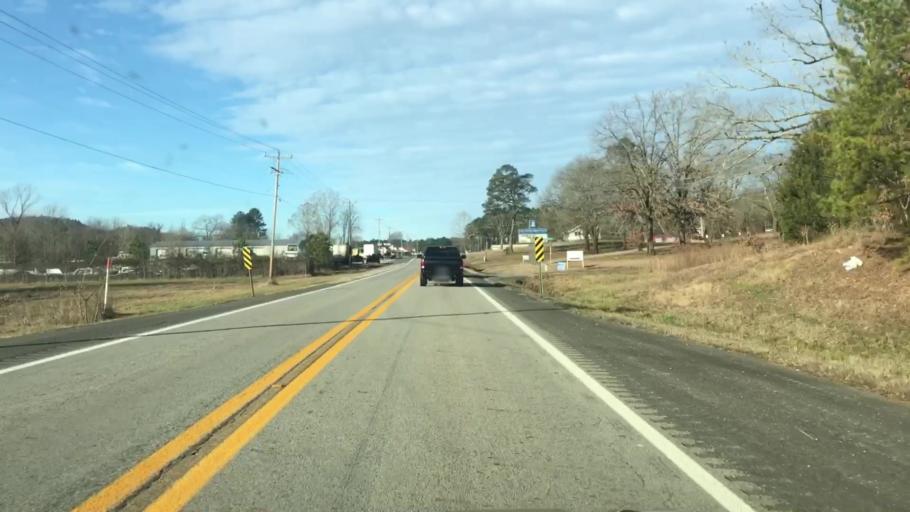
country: US
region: Arkansas
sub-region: Montgomery County
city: Mount Ida
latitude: 34.5312
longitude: -93.5240
